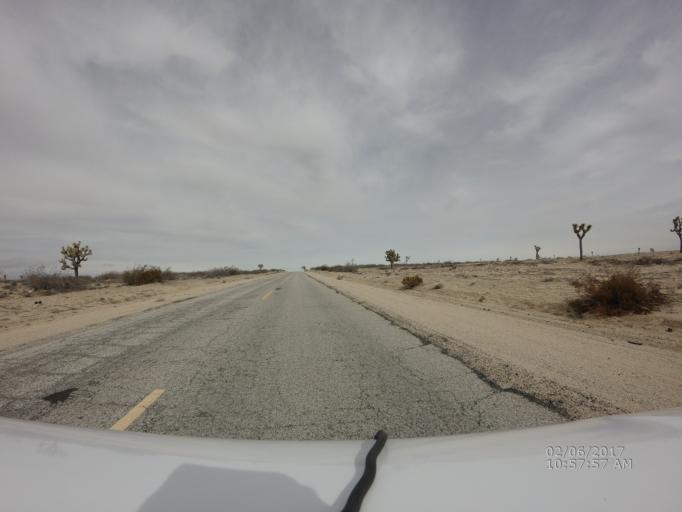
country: US
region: California
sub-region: Los Angeles County
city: Lake Los Angeles
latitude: 34.6253
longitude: -117.7027
